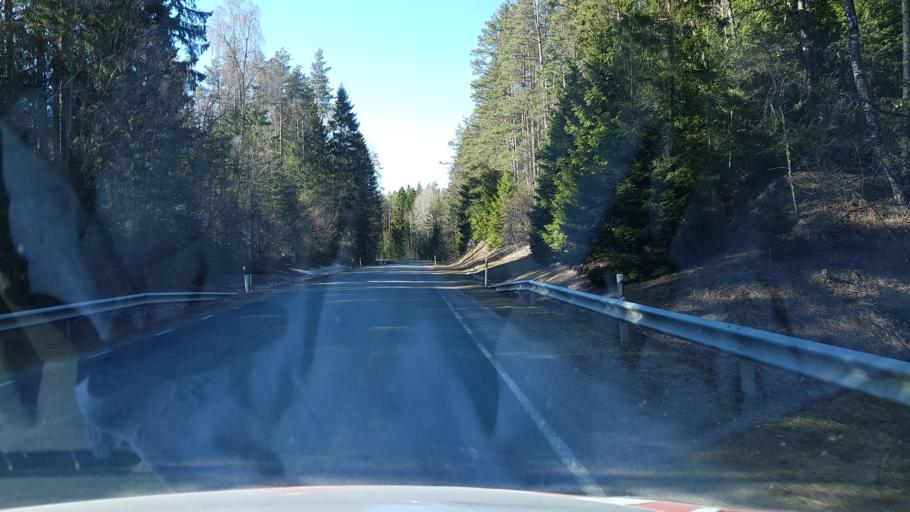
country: EE
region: Laeaene-Virumaa
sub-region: Vinni vald
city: Vinni
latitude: 59.2700
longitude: 26.6640
